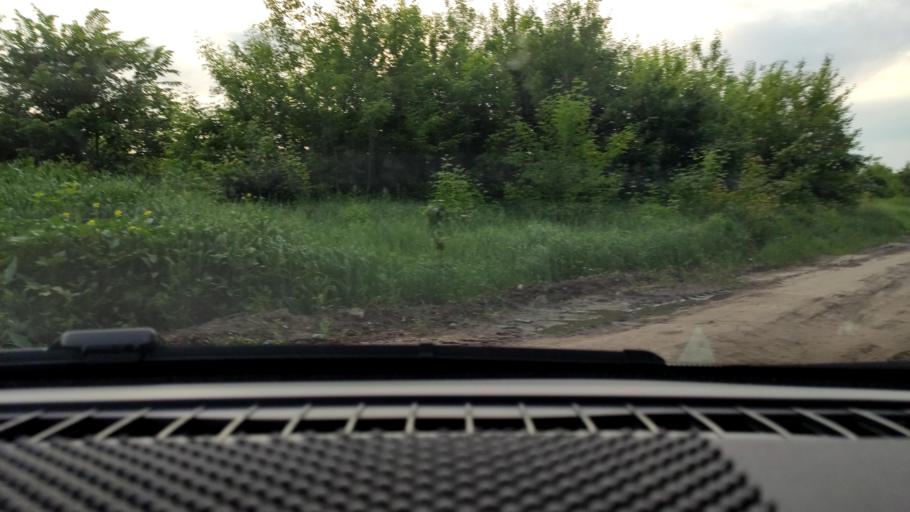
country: RU
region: Voronezj
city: Podgornoye
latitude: 51.7194
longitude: 39.1906
